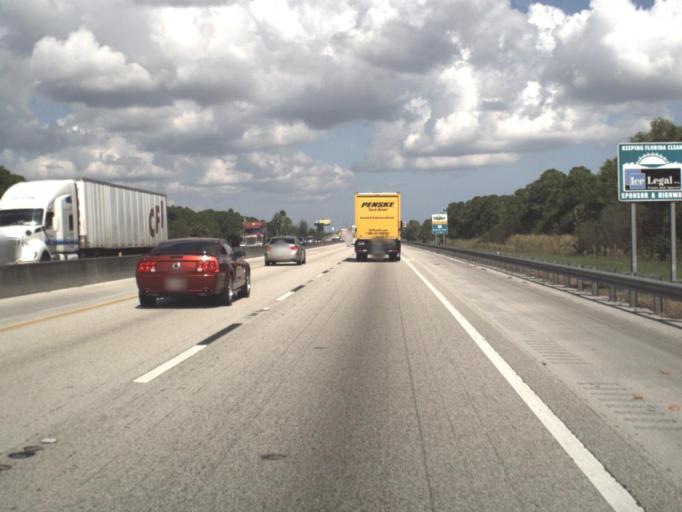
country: US
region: Florida
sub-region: Palm Beach County
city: Palm Beach Gardens
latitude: 26.7872
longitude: -80.1320
